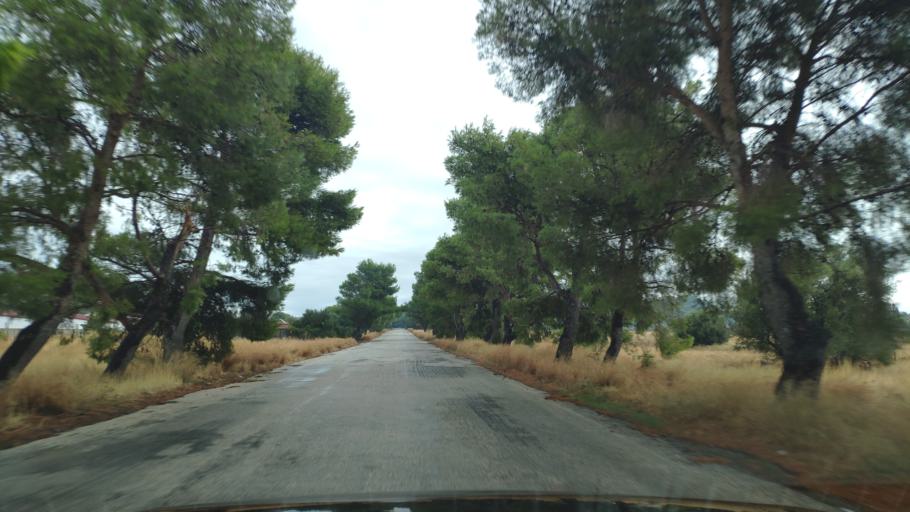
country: GR
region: Peloponnese
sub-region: Nomos Korinthias
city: Loutraki
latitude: 37.9656
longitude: 22.9899
